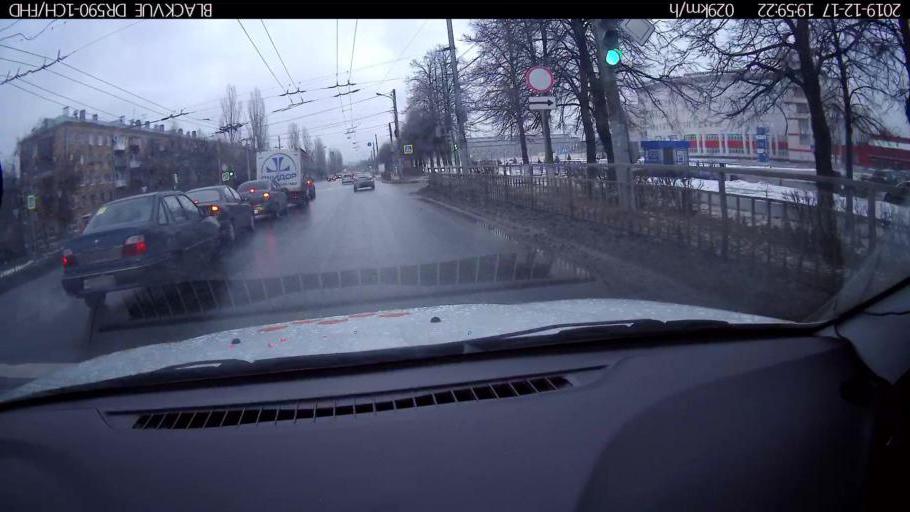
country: RU
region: Nizjnij Novgorod
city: Nizhniy Novgorod
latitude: 56.3283
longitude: 43.9074
